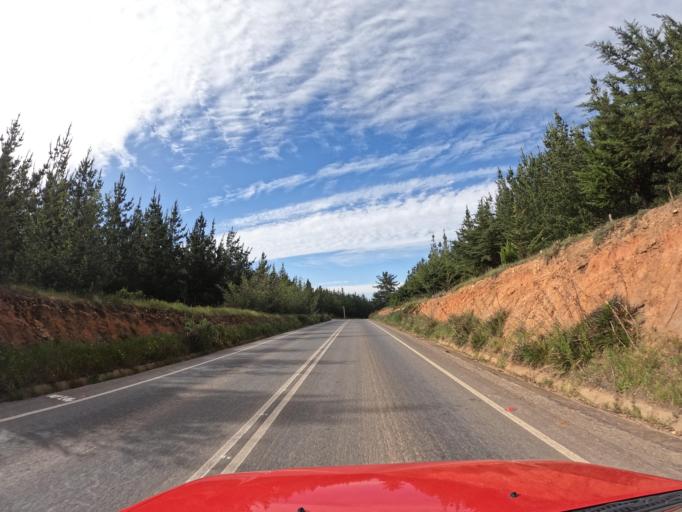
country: CL
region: O'Higgins
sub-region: Provincia de Colchagua
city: Santa Cruz
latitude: -34.3250
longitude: -71.8715
